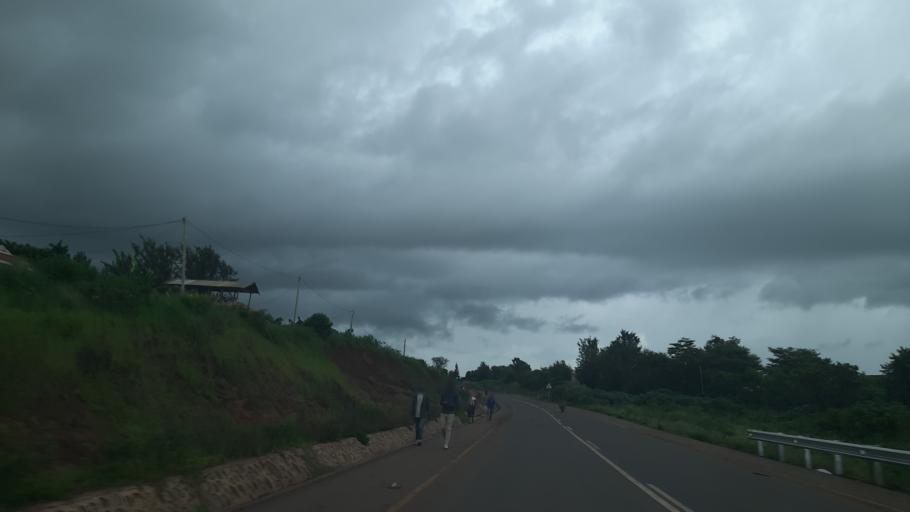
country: TZ
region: Arusha
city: Arusha
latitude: -3.4448
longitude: 36.7024
